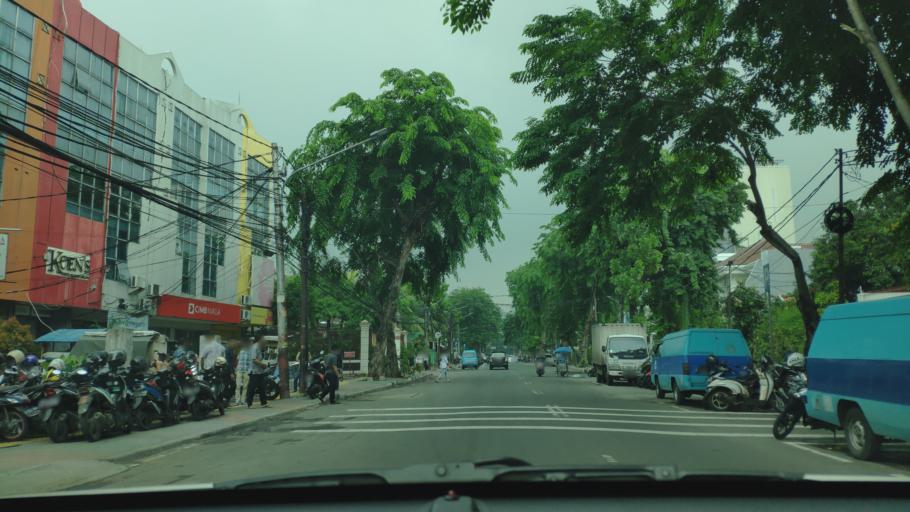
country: ID
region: Jakarta Raya
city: Jakarta
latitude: -6.1676
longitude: 106.8140
